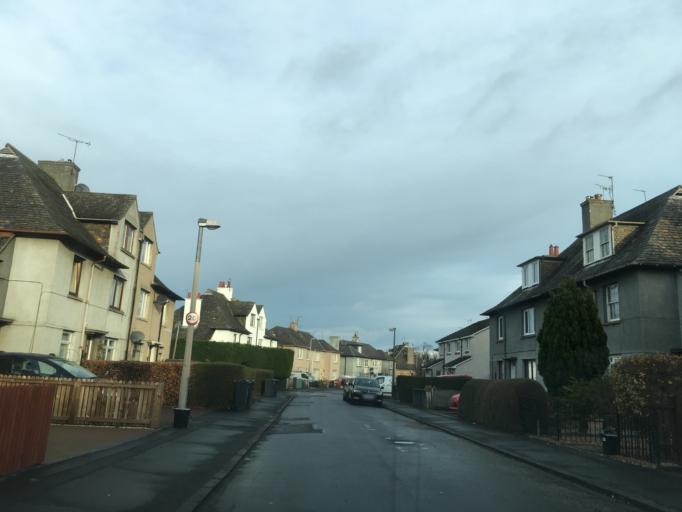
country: GB
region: Scotland
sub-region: Edinburgh
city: Colinton
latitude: 55.9308
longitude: -3.2486
